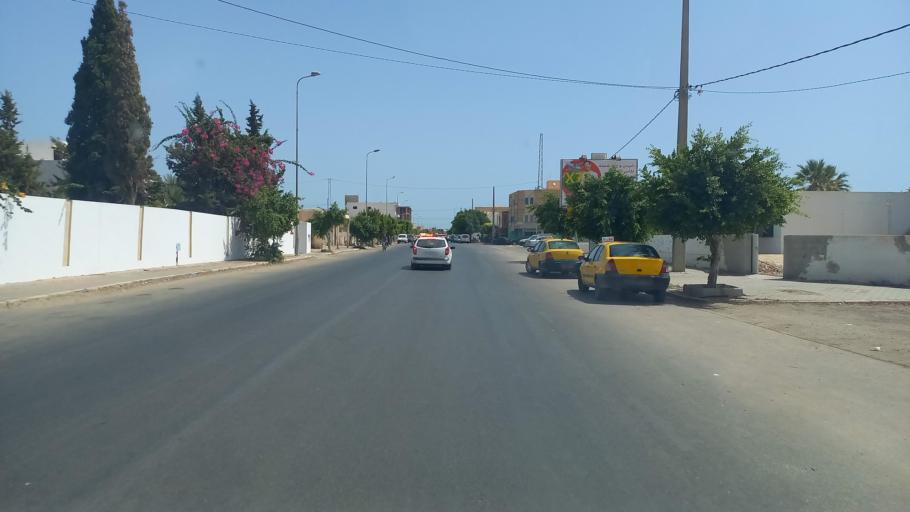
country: TN
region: Madanin
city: Zarzis
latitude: 33.4953
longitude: 11.0845
